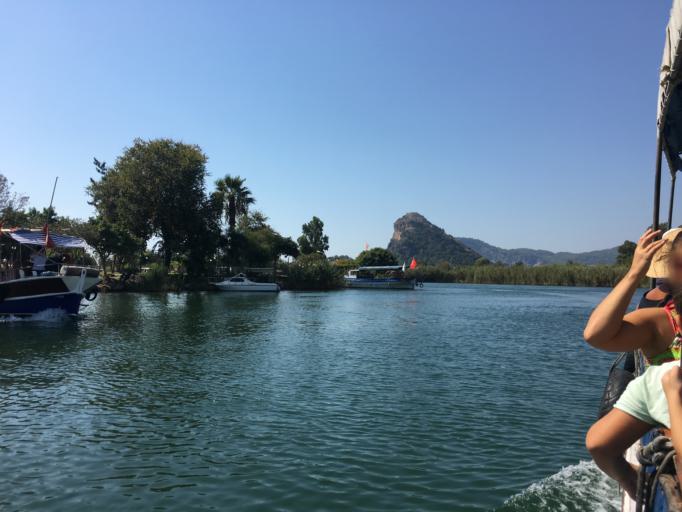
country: TR
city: Dalyan
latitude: 36.8329
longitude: 28.6383
